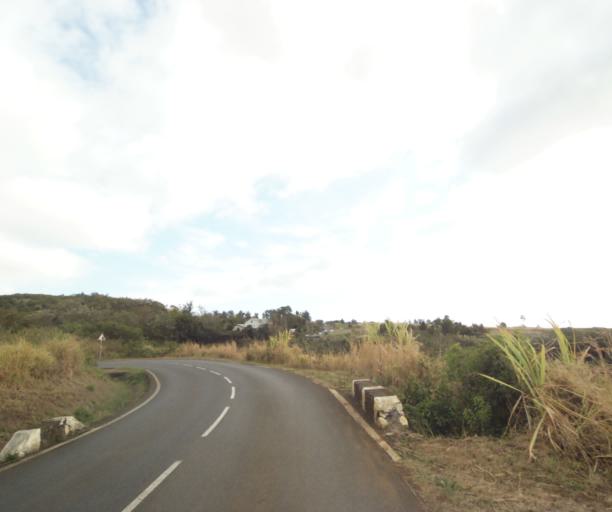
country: RE
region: Reunion
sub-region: Reunion
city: Trois-Bassins
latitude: -21.0635
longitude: 55.2796
